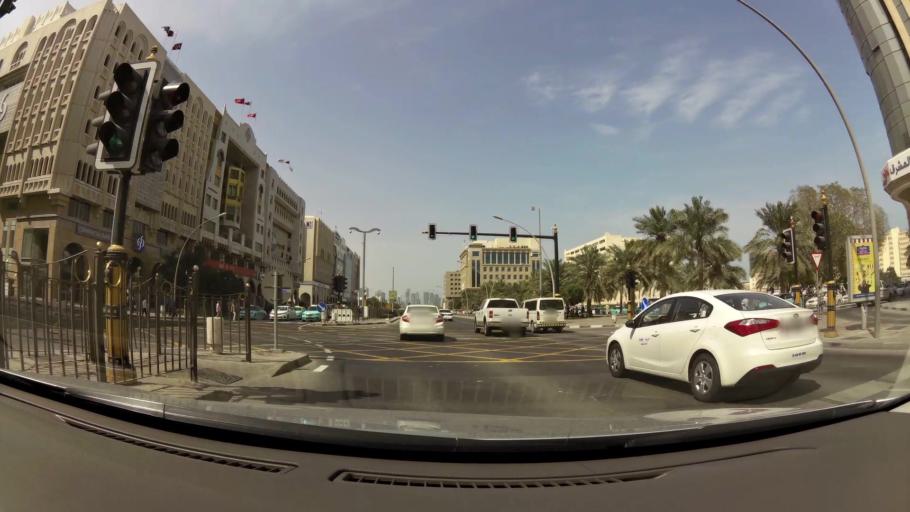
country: QA
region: Baladiyat ad Dawhah
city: Doha
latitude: 25.2824
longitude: 51.5350
